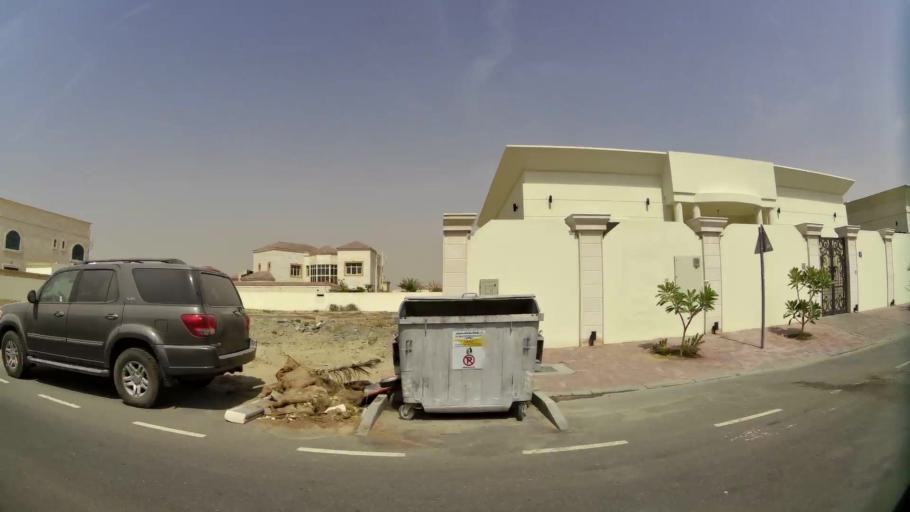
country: AE
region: Ash Shariqah
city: Sharjah
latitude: 25.2482
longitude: 55.4866
